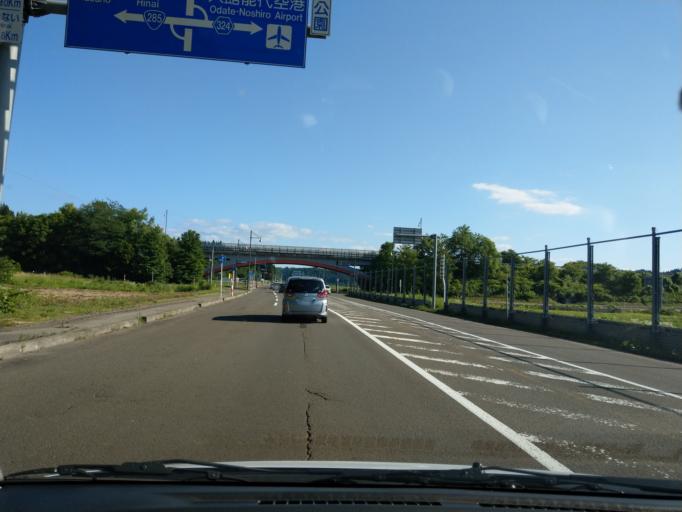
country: JP
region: Akita
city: Takanosu
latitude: 40.1894
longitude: 140.4007
